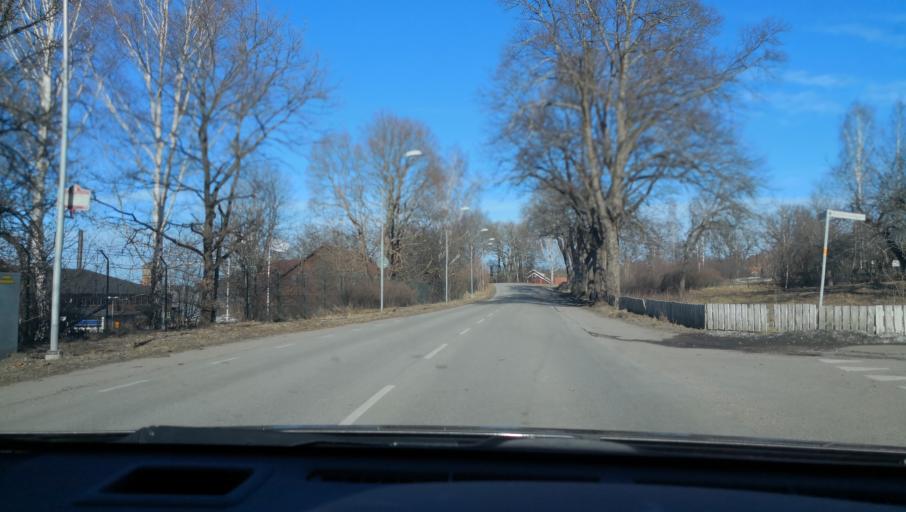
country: SE
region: Uppsala
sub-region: Osthammars Kommun
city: Osterbybruk
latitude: 60.2009
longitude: 17.8972
